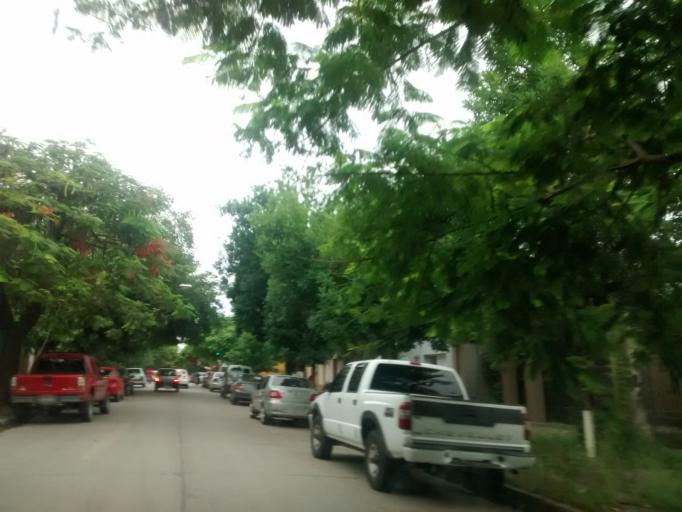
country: AR
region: Chaco
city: Resistencia
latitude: -27.4563
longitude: -58.9790
